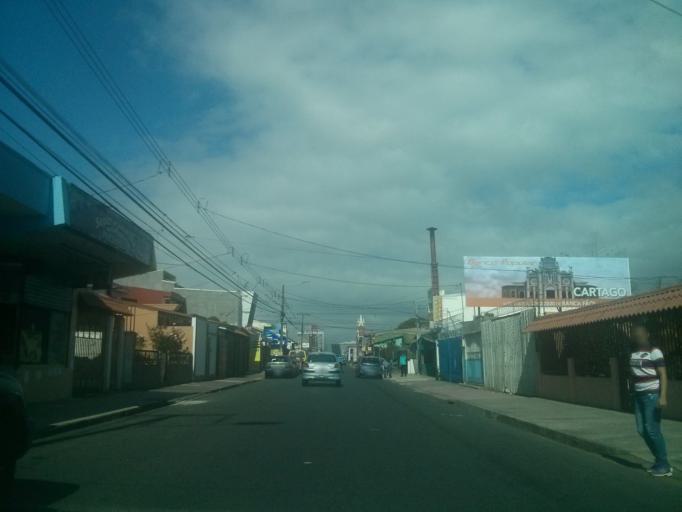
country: CR
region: Cartago
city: Cartago
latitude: 9.8659
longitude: -83.9290
